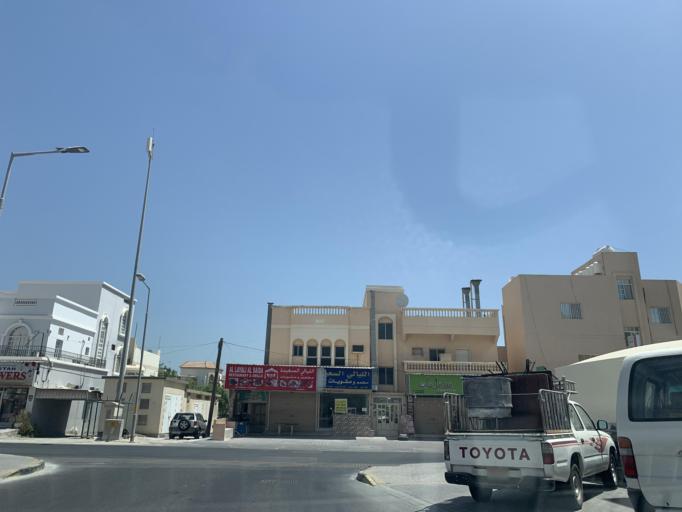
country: BH
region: Northern
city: Ar Rifa'
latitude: 26.1348
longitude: 50.5776
